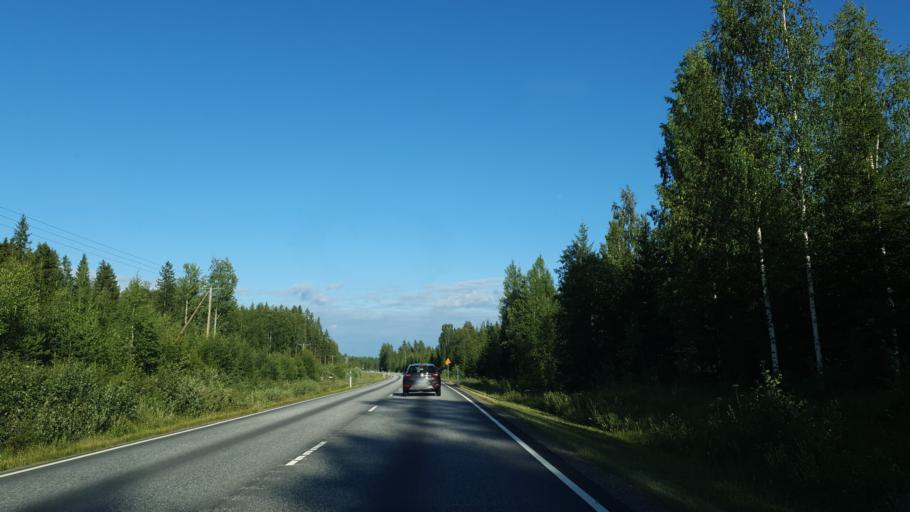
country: FI
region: North Karelia
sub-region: Joensuu
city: Outokumpu
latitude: 62.5333
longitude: 28.9593
